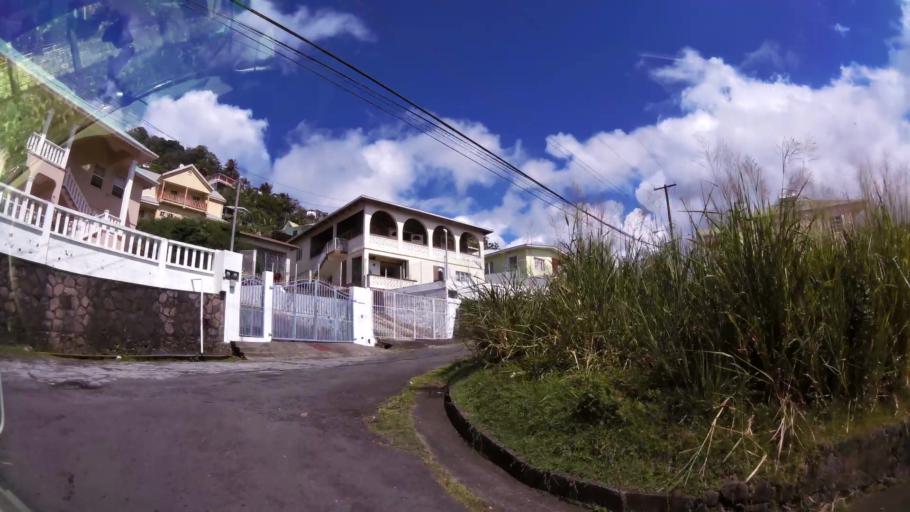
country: VC
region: Saint George
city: Kingstown Park
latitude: 13.1635
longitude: -61.2313
